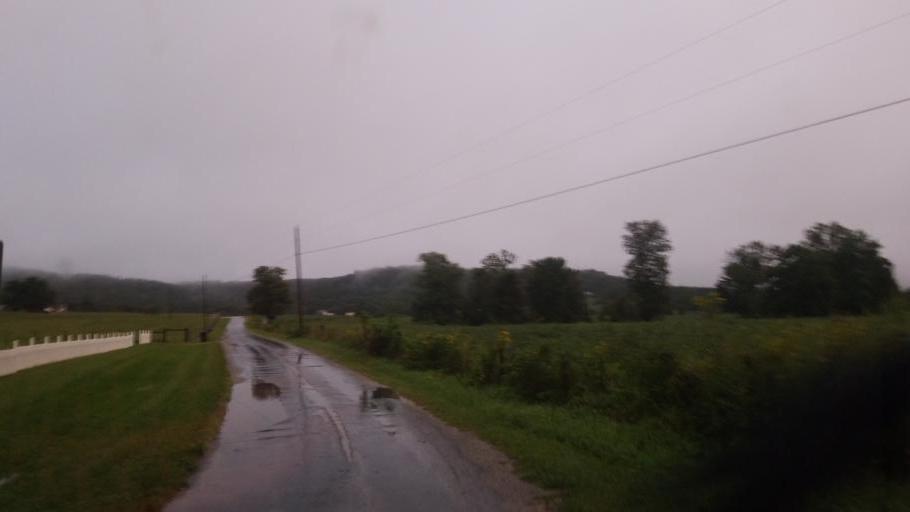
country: US
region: Kentucky
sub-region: Fleming County
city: Flemingsburg
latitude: 38.4483
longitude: -83.6258
